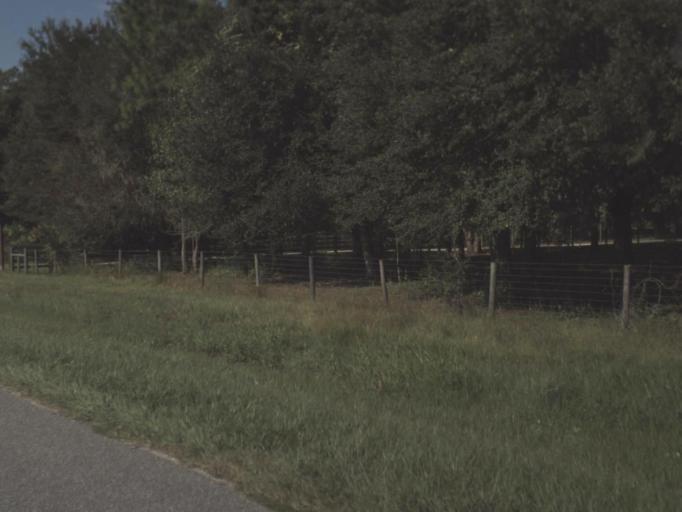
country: US
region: Florida
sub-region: Highlands County
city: Avon Park
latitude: 27.5723
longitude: -81.6254
